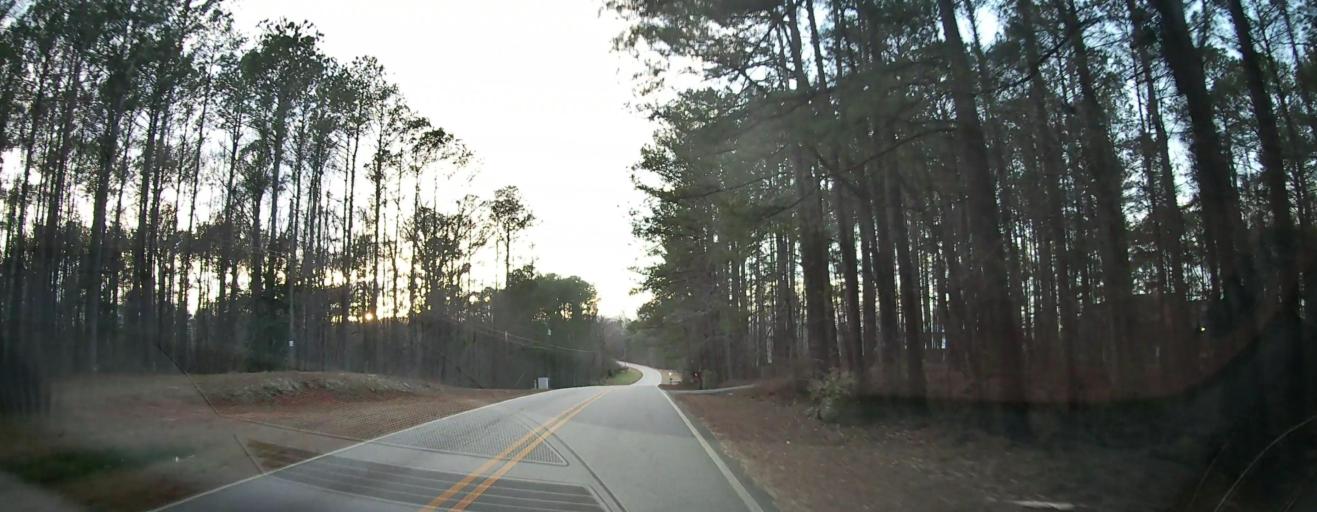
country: US
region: Georgia
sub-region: Harris County
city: Hamilton
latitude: 32.6000
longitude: -84.8866
